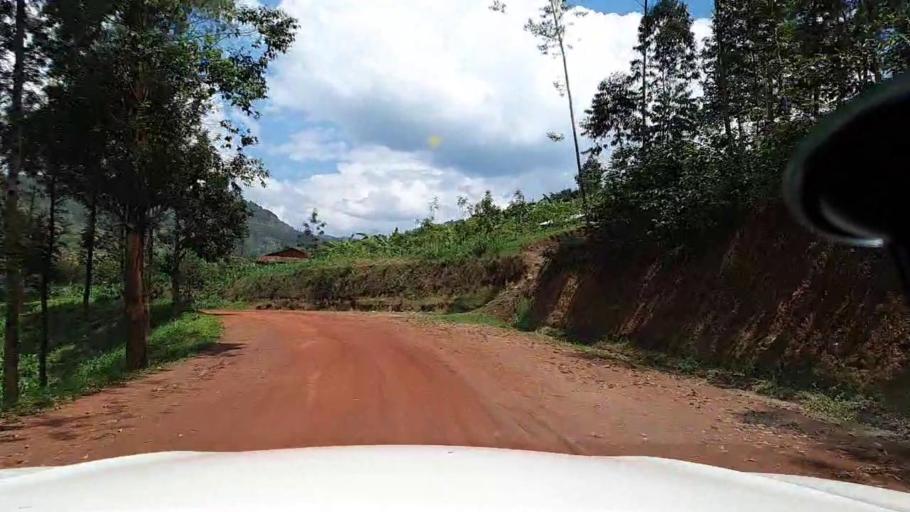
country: RW
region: Northern Province
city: Byumba
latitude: -1.6913
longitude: 29.8268
